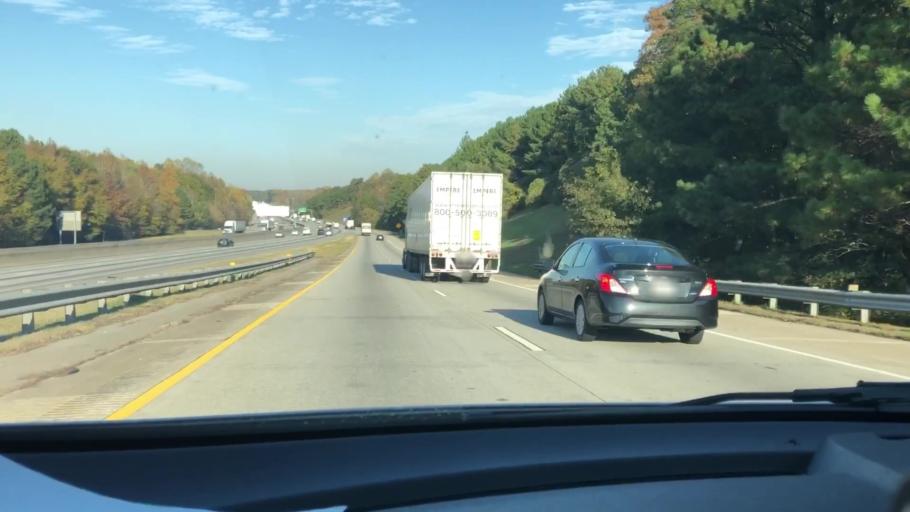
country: US
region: Georgia
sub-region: DeKalb County
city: Gresham Park
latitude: 33.6748
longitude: -84.3228
